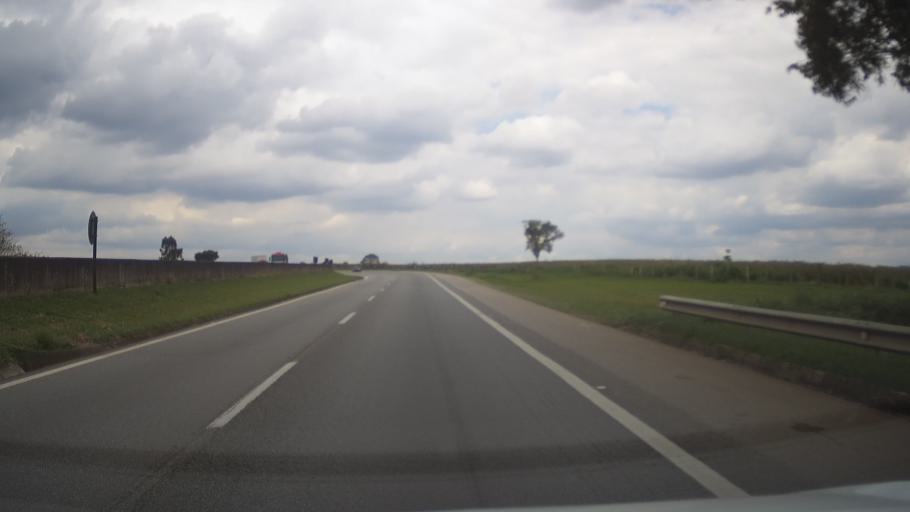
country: BR
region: Minas Gerais
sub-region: Tres Coracoes
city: Tres Coracoes
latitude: -21.4903
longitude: -45.2086
